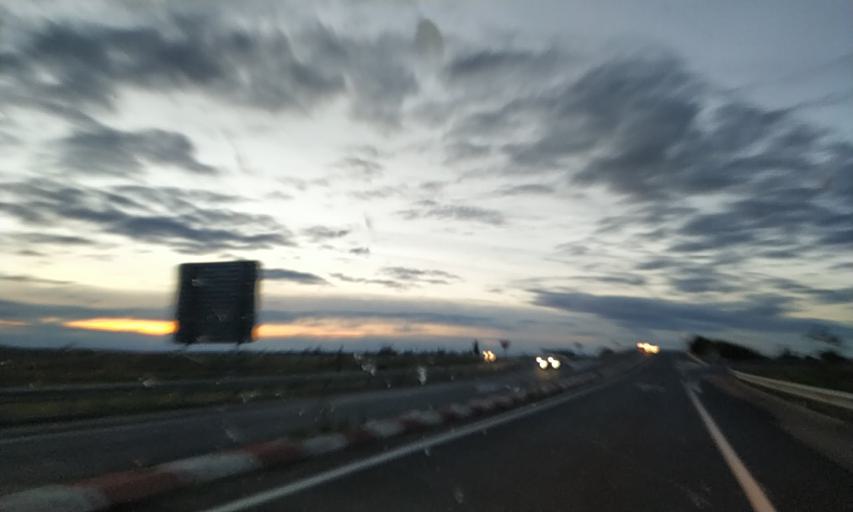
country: ES
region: Extremadura
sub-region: Provincia de Badajoz
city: Badajoz
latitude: 38.9180
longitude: -6.9625
